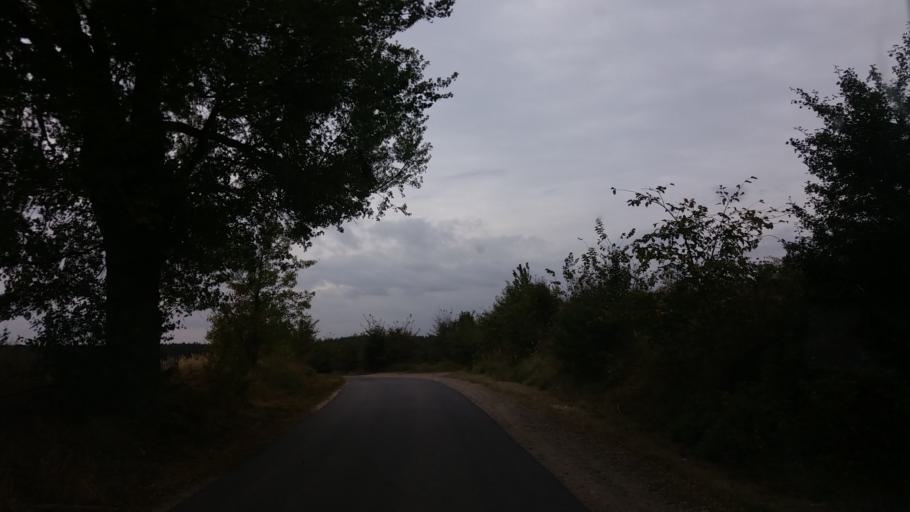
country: PL
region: West Pomeranian Voivodeship
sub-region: Powiat choszczenski
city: Bierzwnik
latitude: 52.9973
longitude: 15.5887
